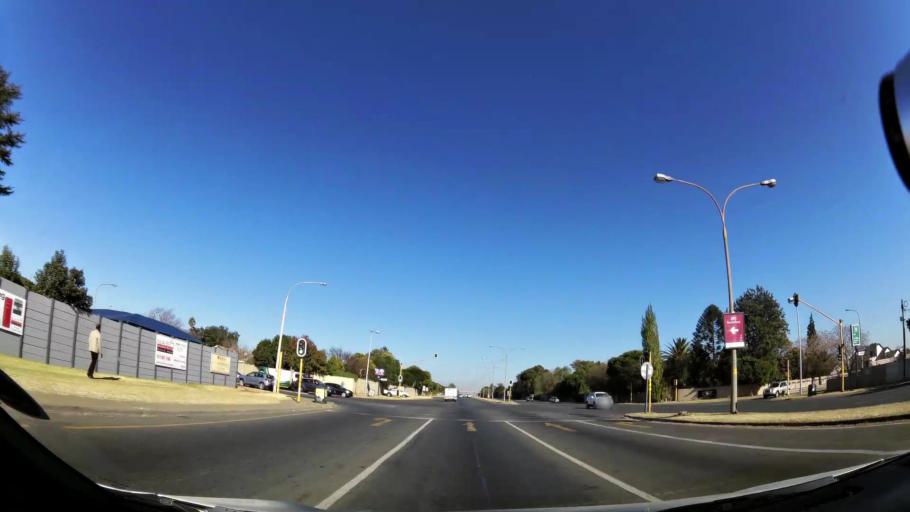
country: ZA
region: Gauteng
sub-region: Ekurhuleni Metropolitan Municipality
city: Germiston
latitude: -26.3079
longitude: 28.1063
